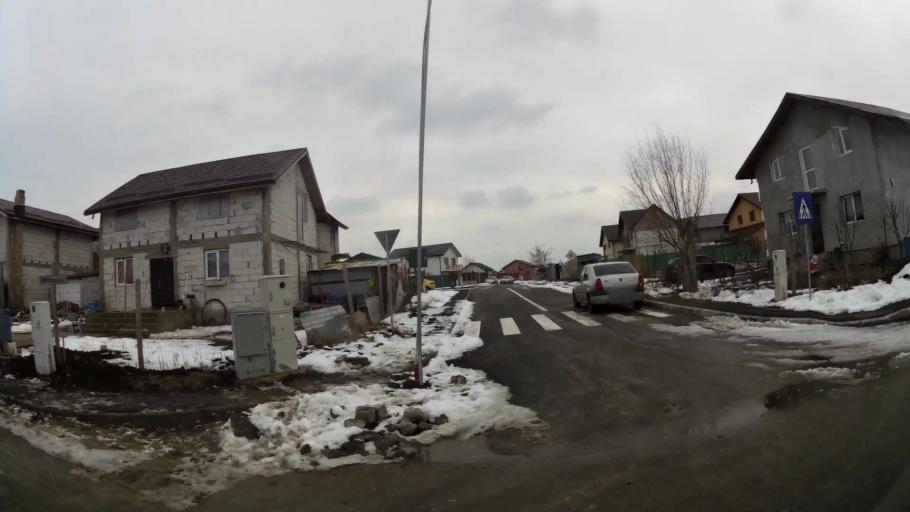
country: RO
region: Ilfov
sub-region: Comuna Tunari
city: Tunari
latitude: 44.5541
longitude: 26.1533
